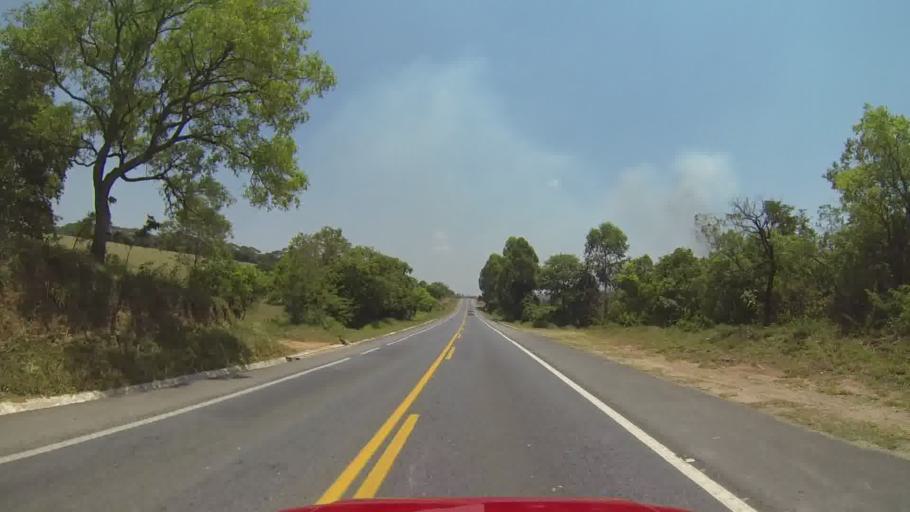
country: BR
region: Minas Gerais
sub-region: Itapecerica
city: Itapecerica
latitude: -20.3424
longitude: -45.2630
